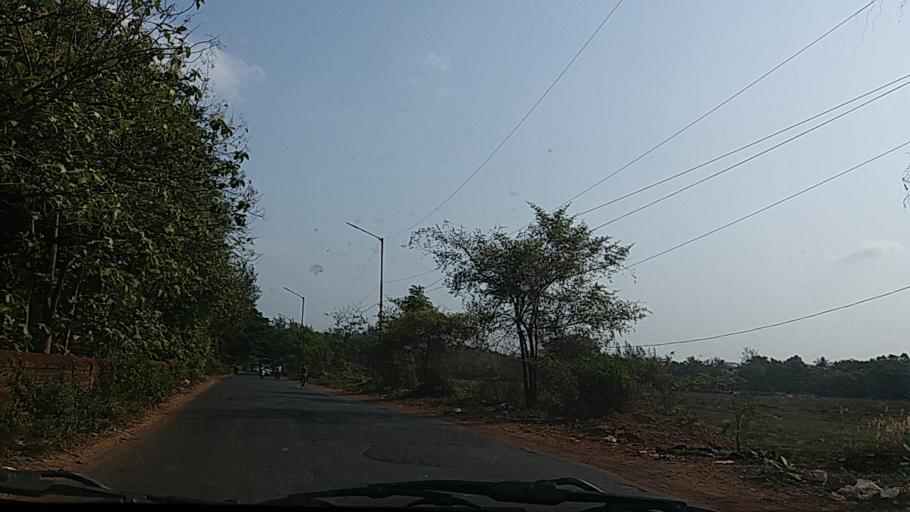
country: IN
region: Goa
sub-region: South Goa
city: Madgaon
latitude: 15.2629
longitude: 73.9701
